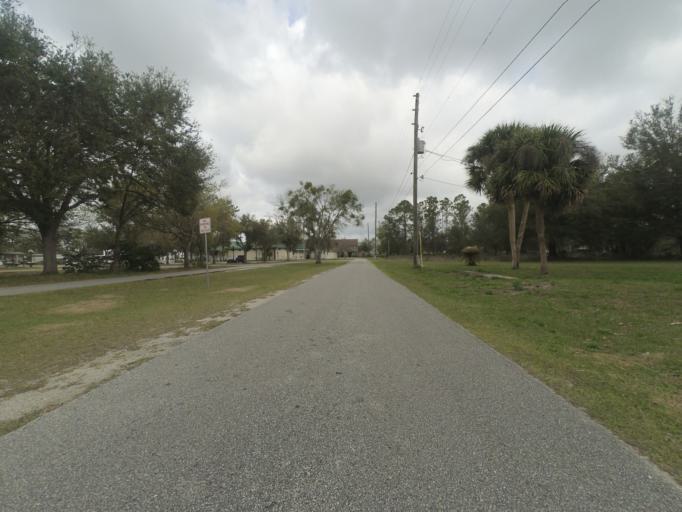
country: US
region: Florida
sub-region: Lake County
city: Umatilla
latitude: 28.9318
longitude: -81.6656
